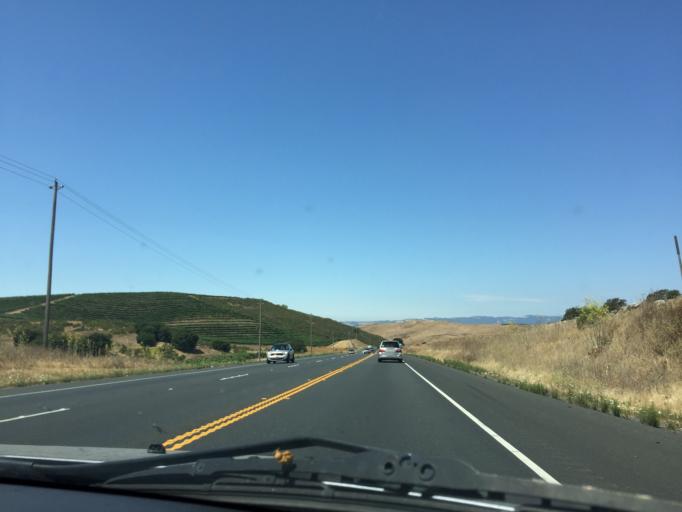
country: US
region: California
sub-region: Sonoma County
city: Sonoma
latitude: 38.2509
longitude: -122.3835
